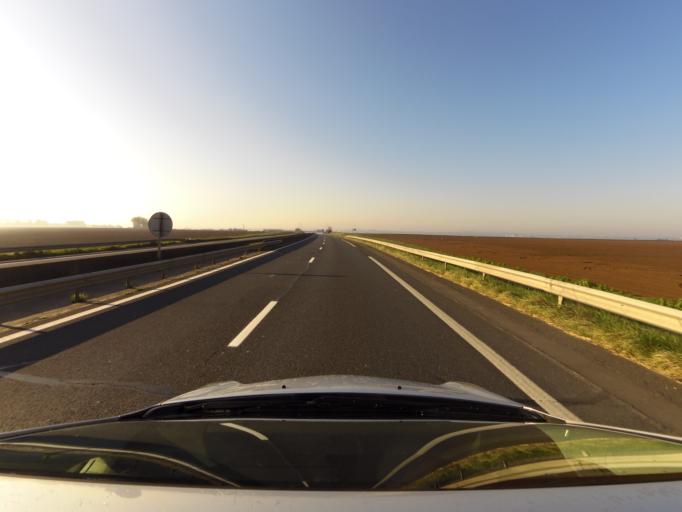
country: FR
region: Lower Normandy
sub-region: Departement du Calvados
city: Bretteville-sur-Odon
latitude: 49.1725
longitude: -0.4299
